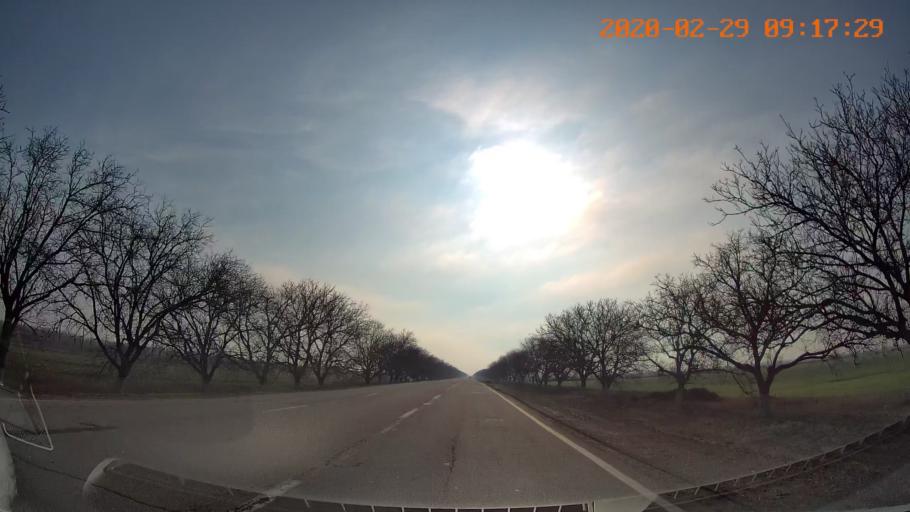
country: MD
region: Telenesti
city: Pervomaisc
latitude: 46.7826
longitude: 29.9050
